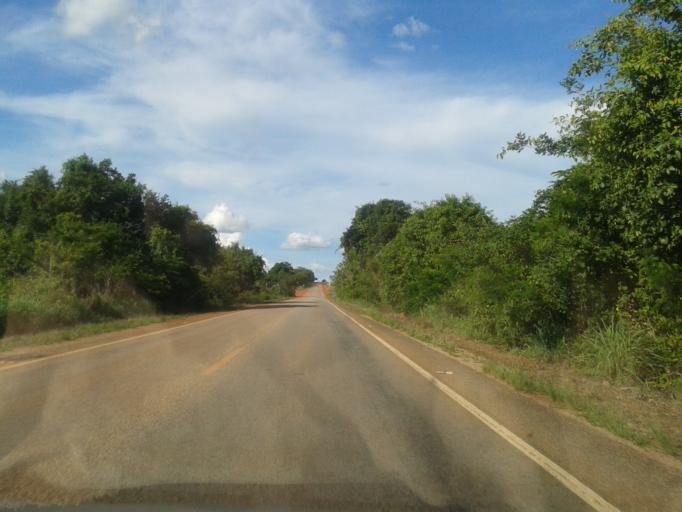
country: BR
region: Goias
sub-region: Mozarlandia
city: Mozarlandia
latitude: -14.4023
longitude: -50.4433
